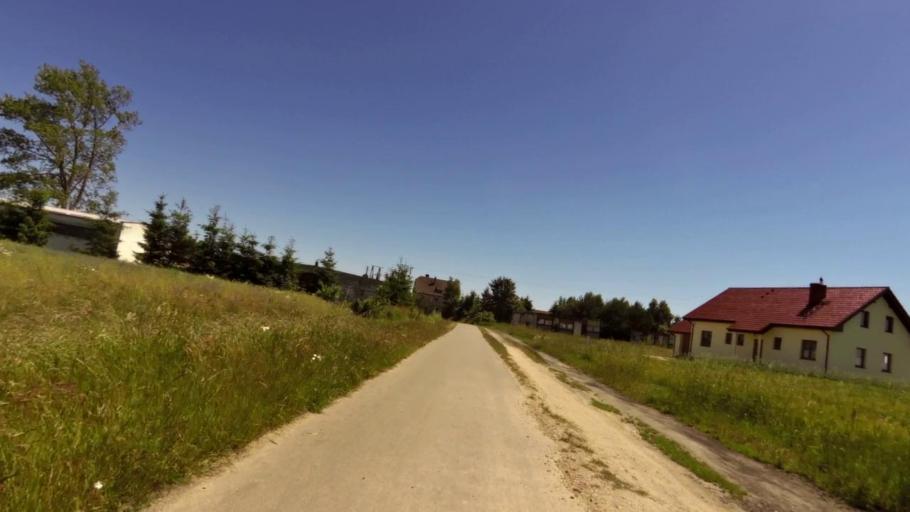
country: PL
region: West Pomeranian Voivodeship
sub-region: Powiat kolobrzeski
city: Kolobrzeg
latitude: 54.0927
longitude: 15.5728
